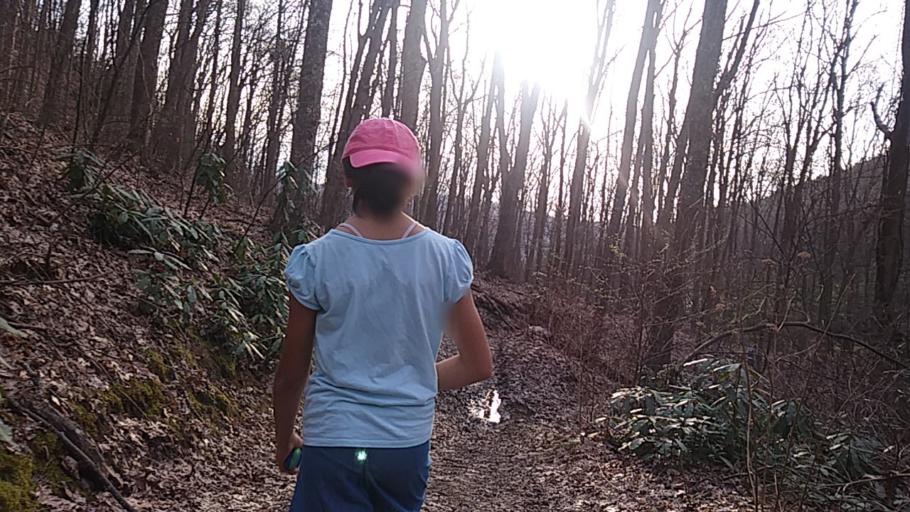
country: US
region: Tennessee
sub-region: Greene County
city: Tusculum
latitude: 36.0645
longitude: -82.6798
